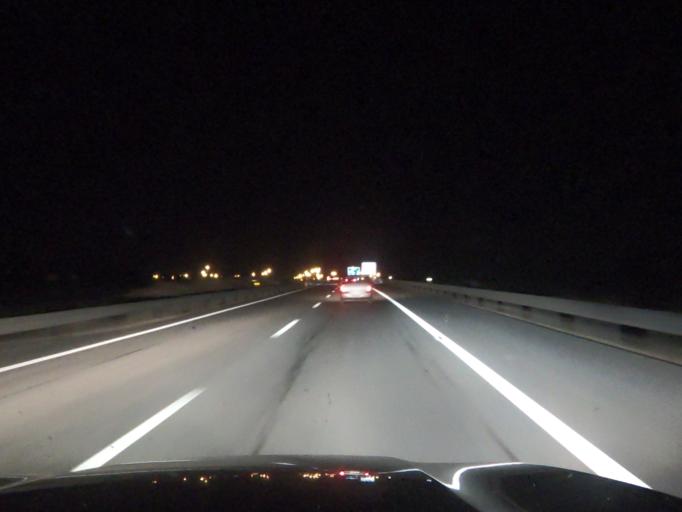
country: PT
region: Beja
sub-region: Almodovar
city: Almodovar
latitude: 37.5284
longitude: -8.1815
